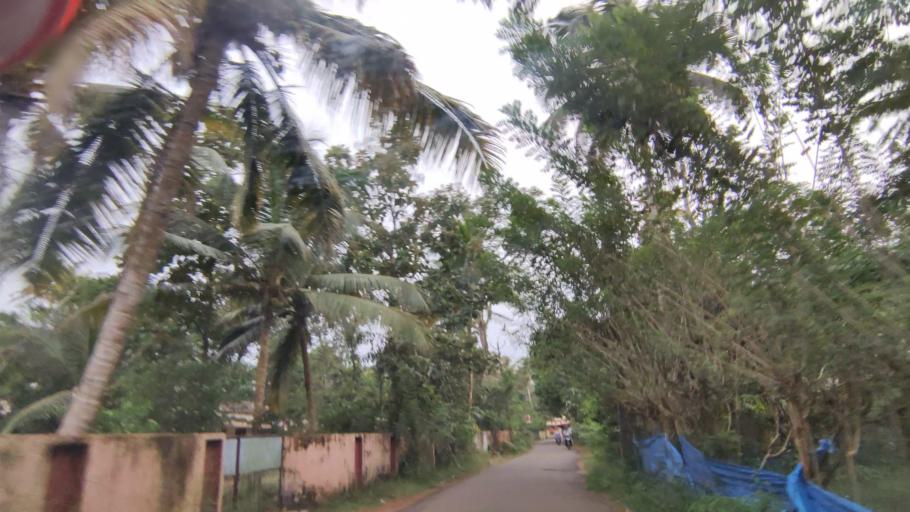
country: IN
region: Kerala
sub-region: Alappuzha
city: Shertallai
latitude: 9.6663
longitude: 76.3662
